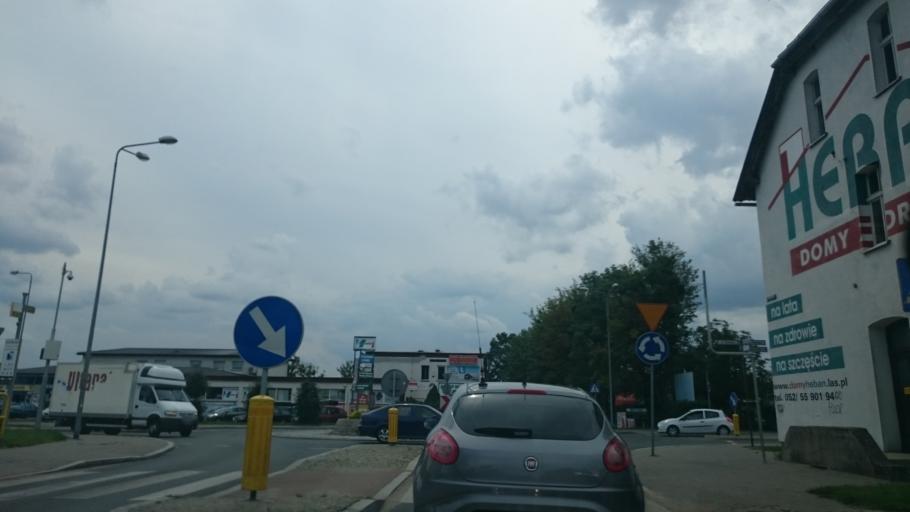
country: PL
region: Kujawsko-Pomorskie
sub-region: Powiat tucholski
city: Tuchola
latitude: 53.5816
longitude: 17.8715
